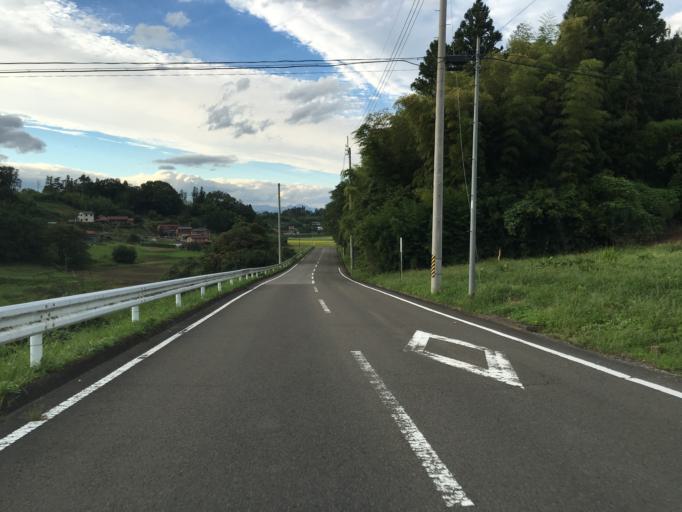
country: JP
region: Fukushima
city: Nihommatsu
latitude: 37.6097
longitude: 140.4964
